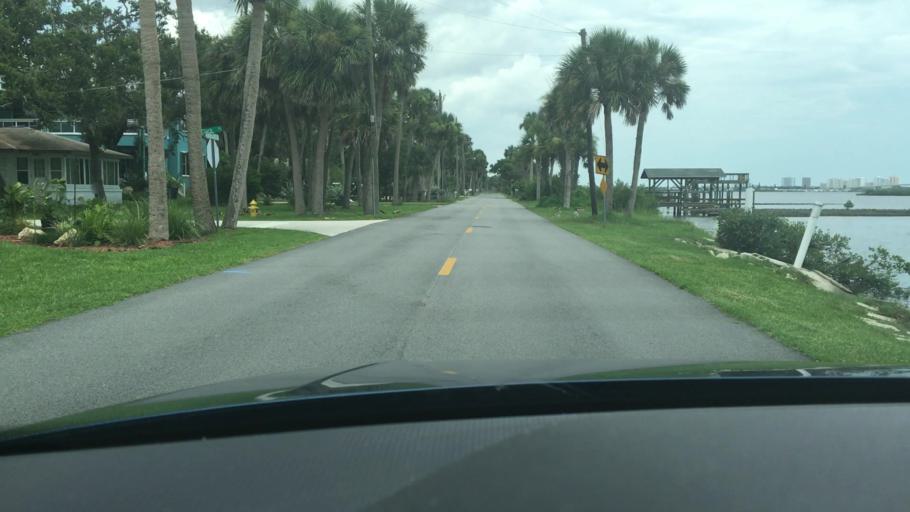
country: US
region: Florida
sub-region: Volusia County
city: Port Orange
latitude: 29.1266
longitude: -80.9771
